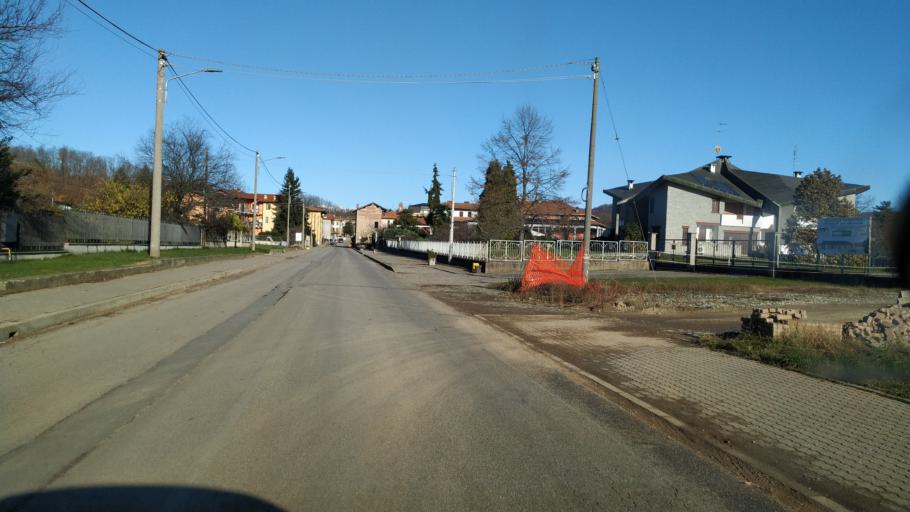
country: IT
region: Piedmont
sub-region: Provincia di Vercelli
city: Lozzolo
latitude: 45.6164
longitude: 8.3232
